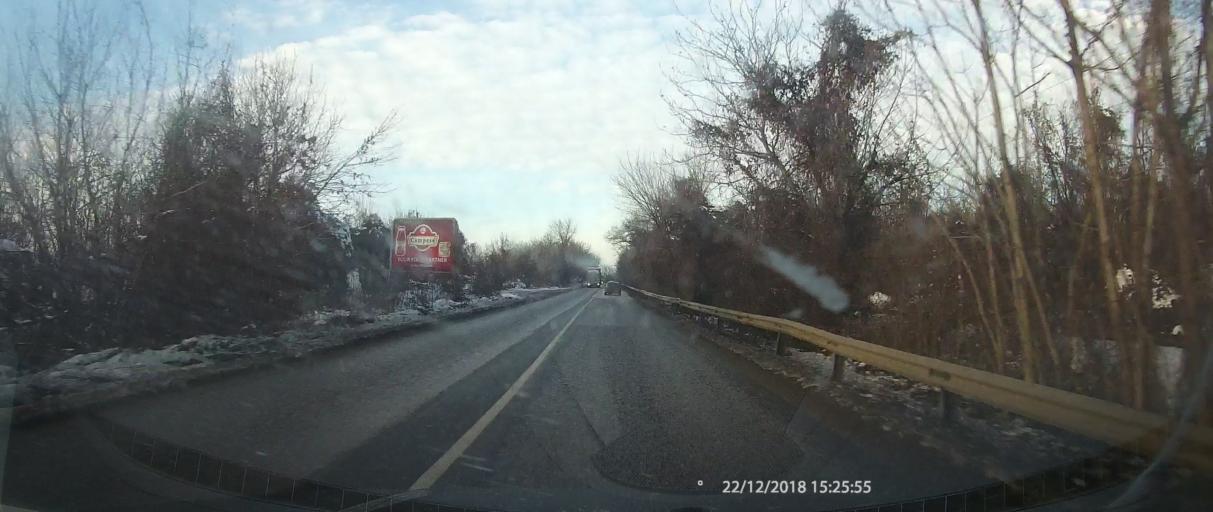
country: RO
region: Giurgiu
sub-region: Comuna Slobozia
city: Slobozia
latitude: 43.7644
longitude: 25.9025
